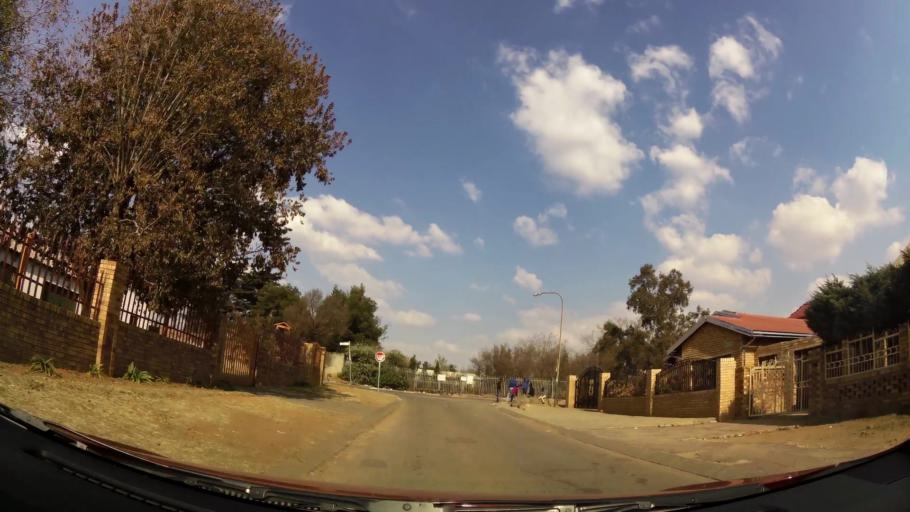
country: ZA
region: Gauteng
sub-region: City of Johannesburg Metropolitan Municipality
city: Soweto
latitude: -26.2402
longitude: 27.9459
